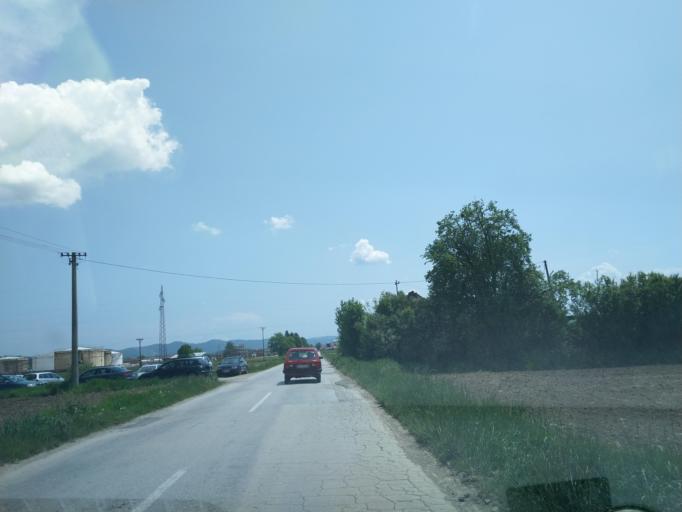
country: RS
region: Central Serbia
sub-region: Zlatiborski Okrug
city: Pozega
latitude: 43.8502
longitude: 20.0065
